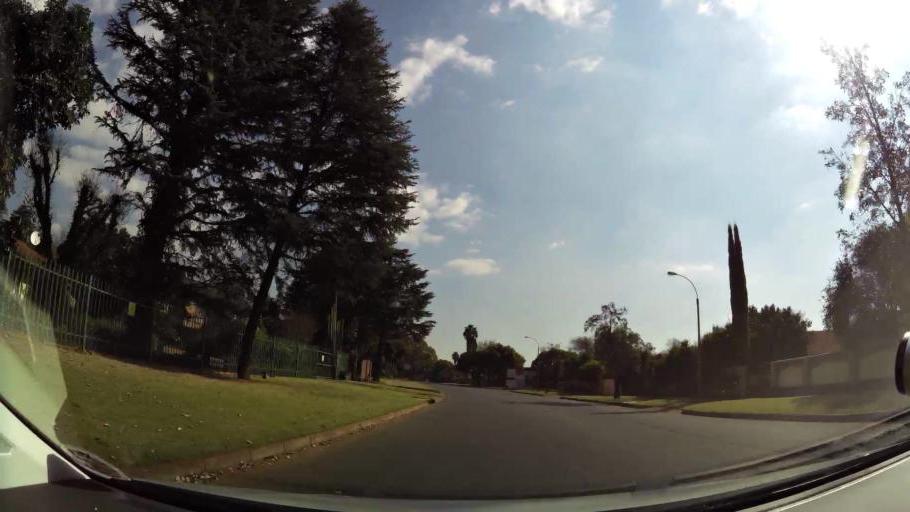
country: ZA
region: Gauteng
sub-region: City of Johannesburg Metropolitan Municipality
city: Modderfontein
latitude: -26.0831
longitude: 28.2337
